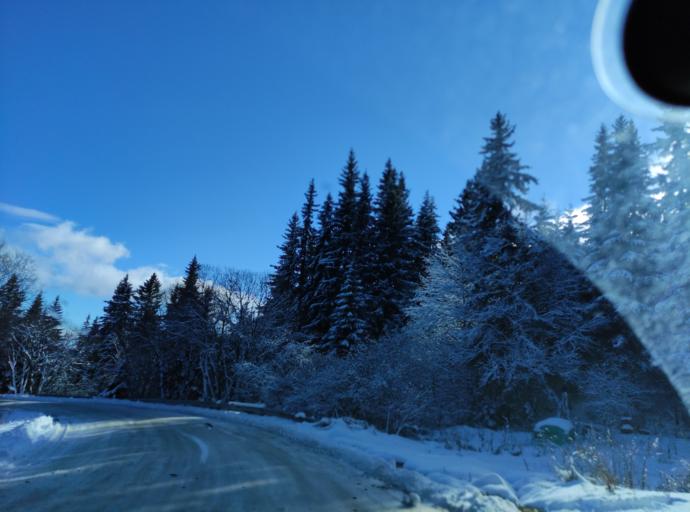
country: BG
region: Sofia-Capital
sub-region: Stolichna Obshtina
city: Sofia
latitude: 42.5872
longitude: 23.2966
